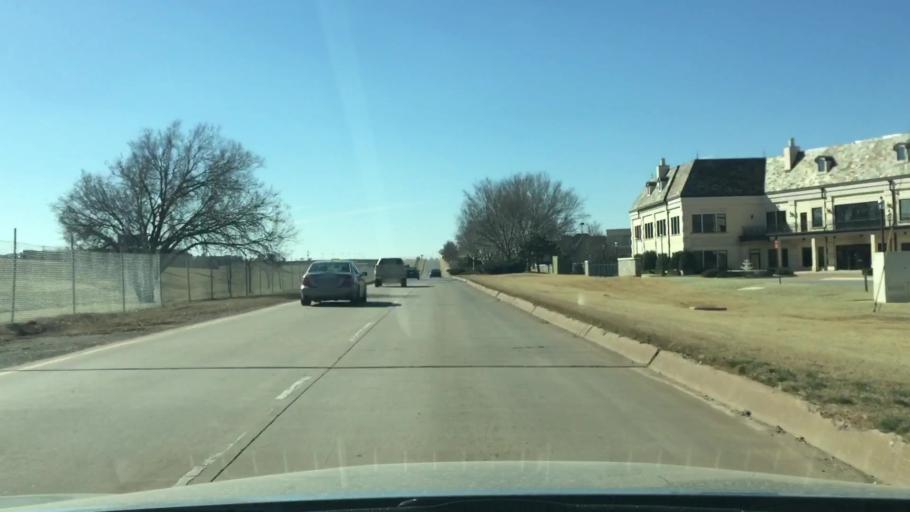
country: US
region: Oklahoma
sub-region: Oklahoma County
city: The Village
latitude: 35.6103
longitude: -97.6060
